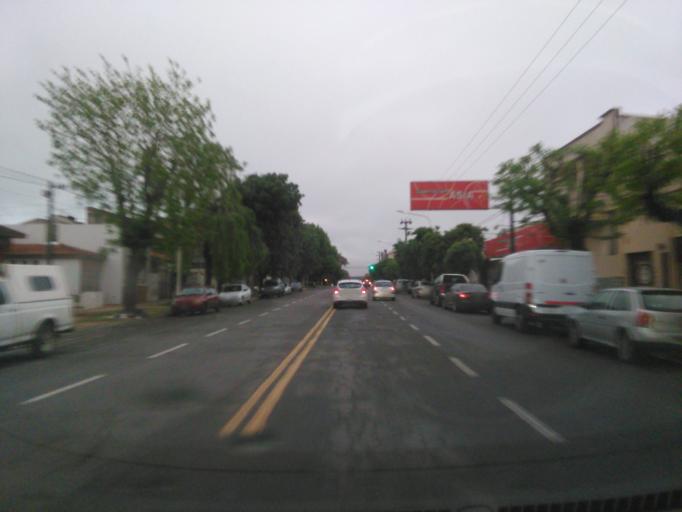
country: AR
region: Buenos Aires
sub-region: Partido de Tandil
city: Tandil
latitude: -37.3320
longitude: -59.1435
